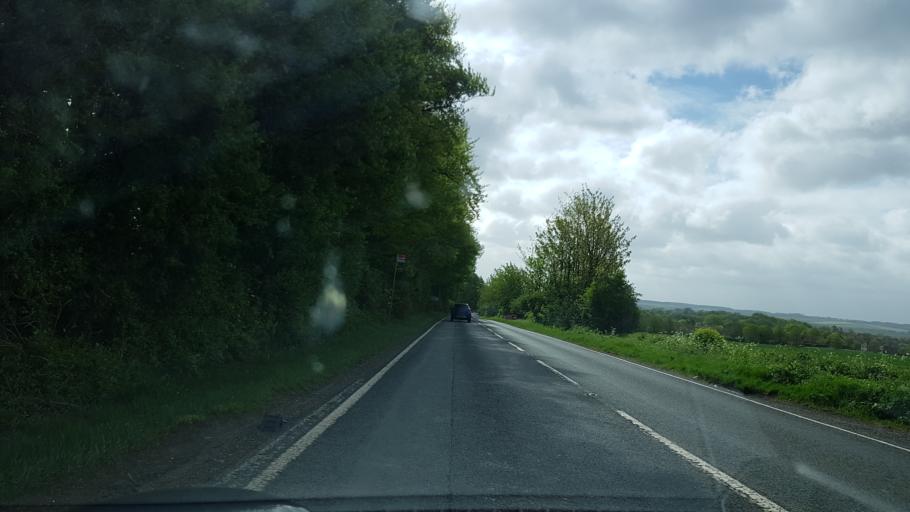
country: GB
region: England
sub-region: Hampshire
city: Basingstoke
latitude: 51.2802
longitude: -1.1284
